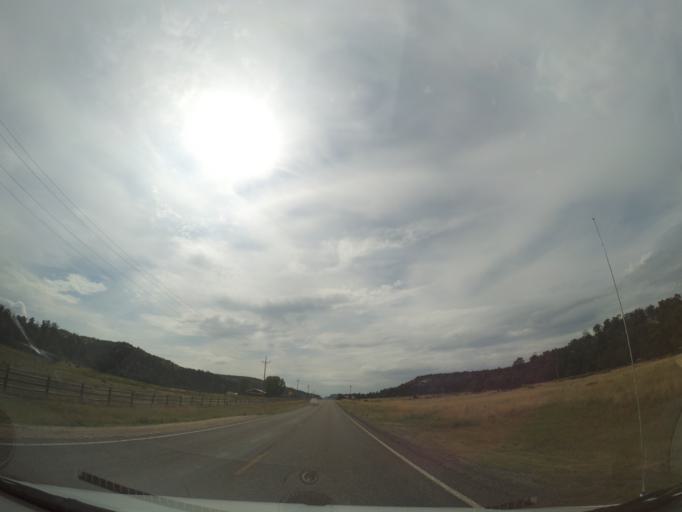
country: US
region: Utah
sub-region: Washington County
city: Hildale
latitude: 37.2397
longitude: -112.8289
